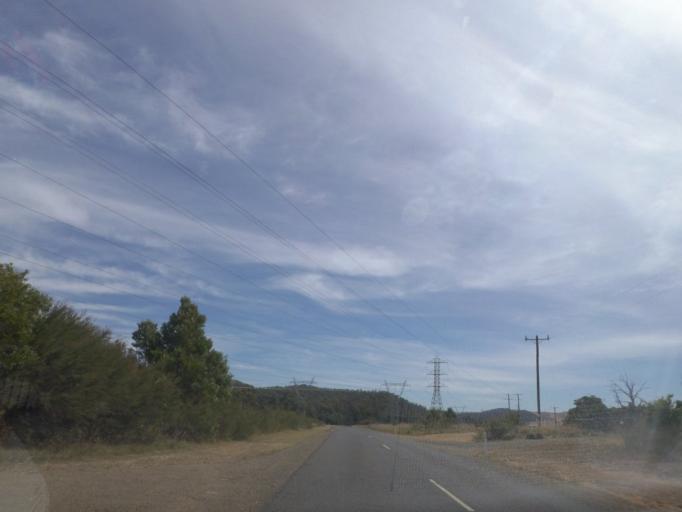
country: AU
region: Victoria
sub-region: Murrindindi
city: Kinglake West
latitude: -37.4629
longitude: 145.3989
